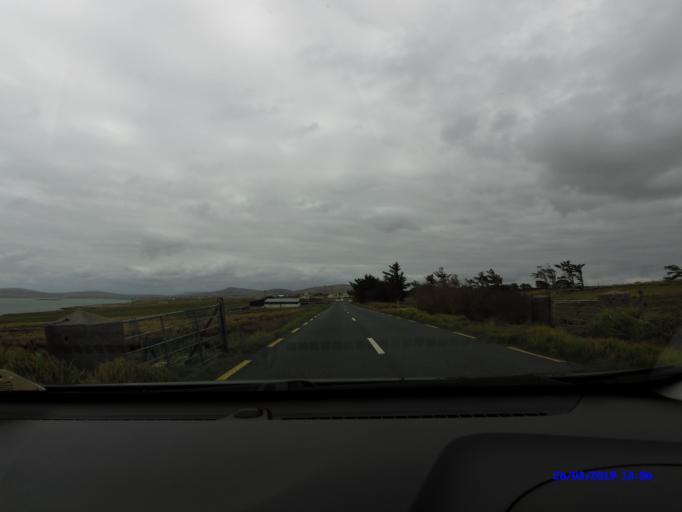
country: IE
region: Connaught
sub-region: Maigh Eo
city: Belmullet
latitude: 54.2106
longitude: -9.9504
